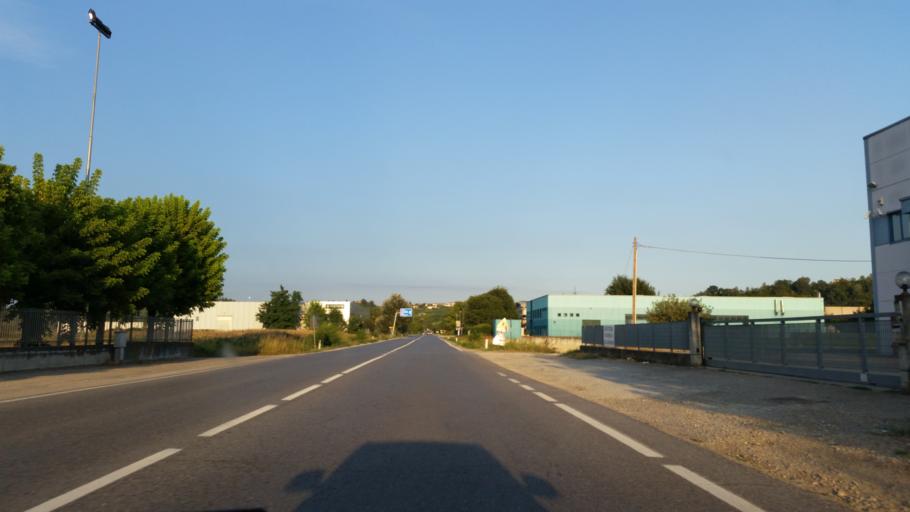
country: IT
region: Piedmont
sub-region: Provincia di Cuneo
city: Sant'Antonio
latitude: 44.7434
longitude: 8.0750
